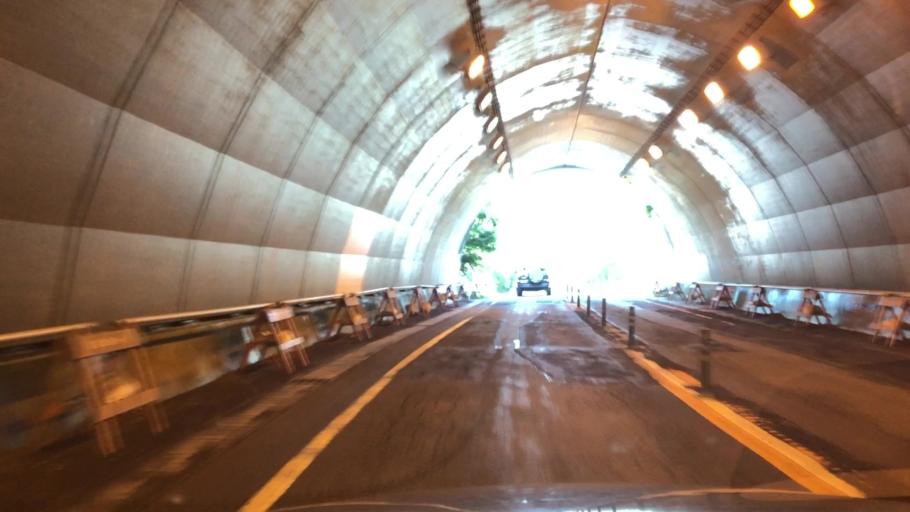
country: JP
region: Shizuoka
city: Gotemba
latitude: 35.3300
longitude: 138.8026
